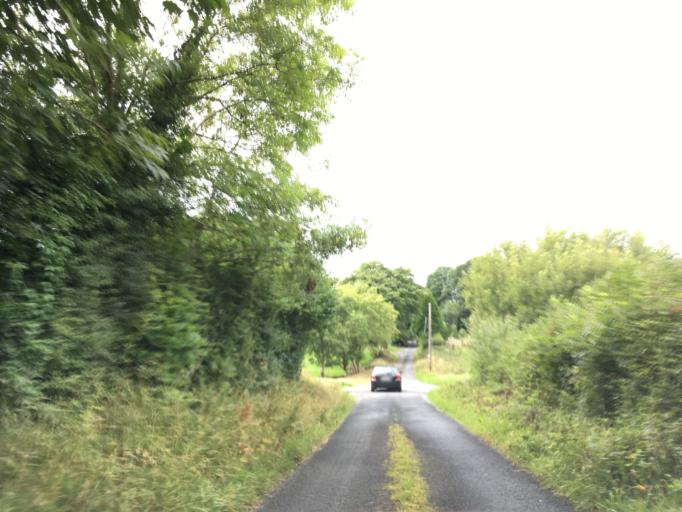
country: IE
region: Munster
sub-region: An Clar
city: Ennis
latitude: 52.7284
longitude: -9.0795
